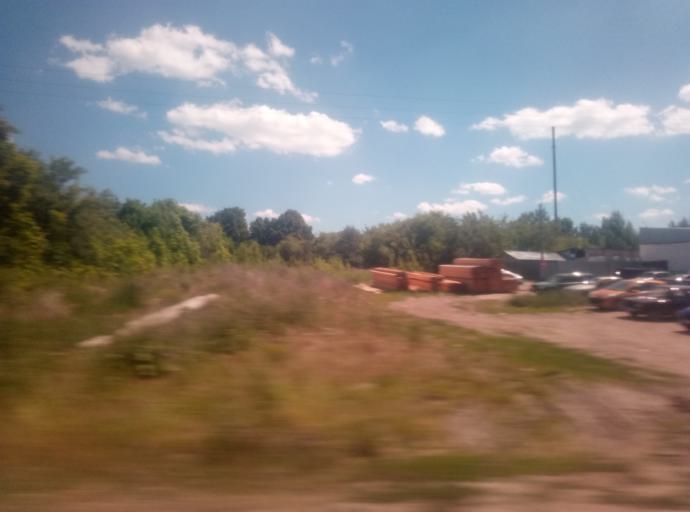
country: RU
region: Tula
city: Kireyevsk
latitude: 53.9348
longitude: 37.9457
